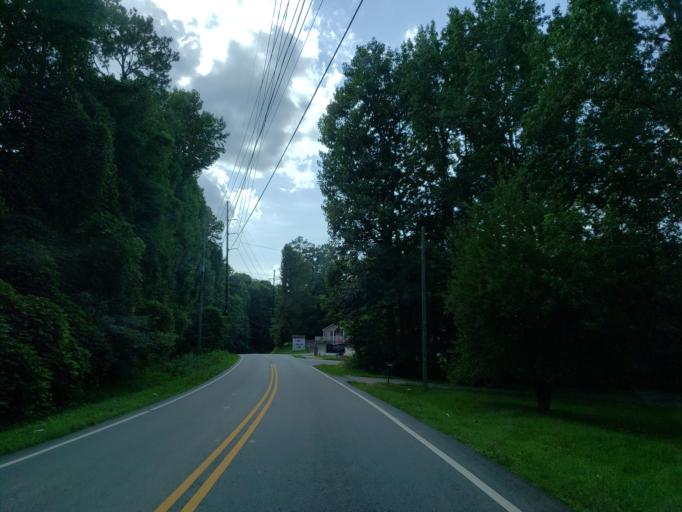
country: US
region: Georgia
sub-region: Cobb County
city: Powder Springs
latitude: 33.8734
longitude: -84.6394
